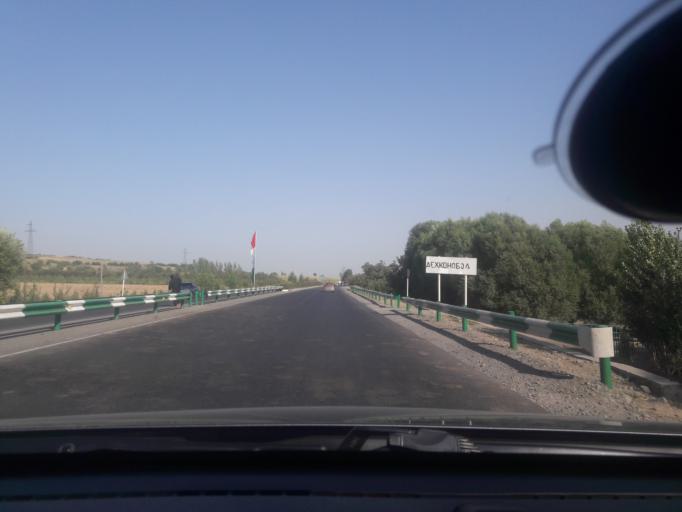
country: TJ
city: Shahrinav
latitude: 38.5742
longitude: 68.3606
